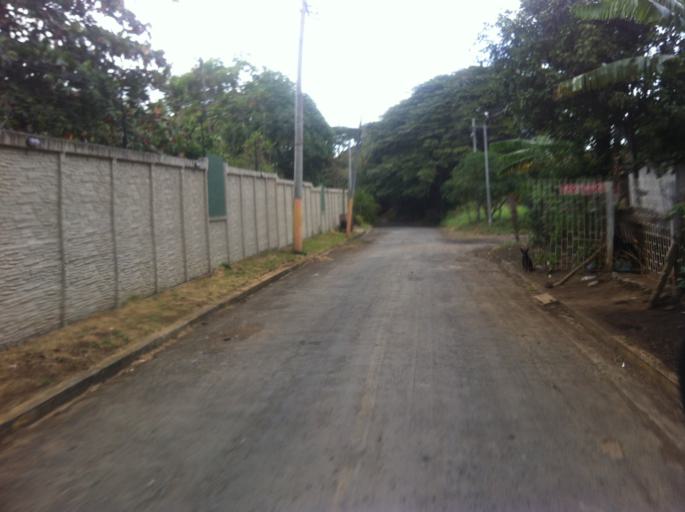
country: NI
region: Managua
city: Ciudad Sandino
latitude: 12.0777
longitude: -86.3235
